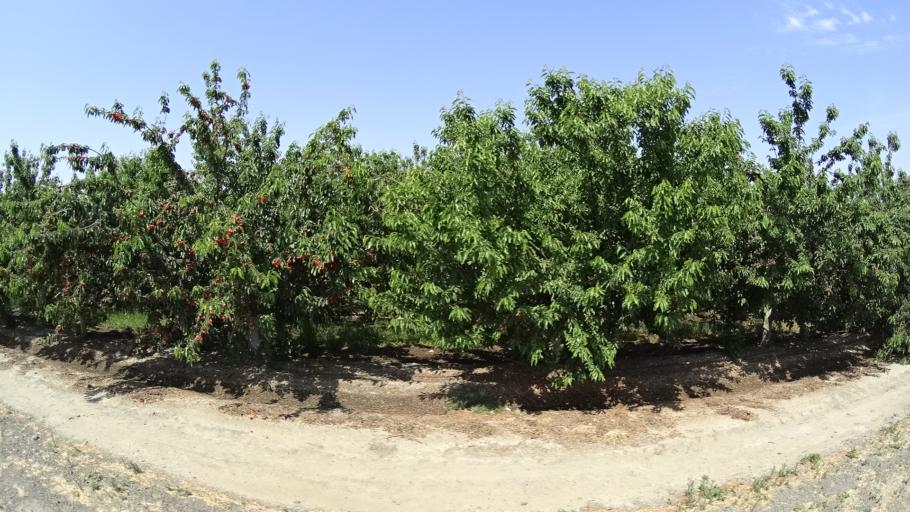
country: US
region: California
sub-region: Kings County
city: Armona
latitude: 36.3505
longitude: -119.7449
